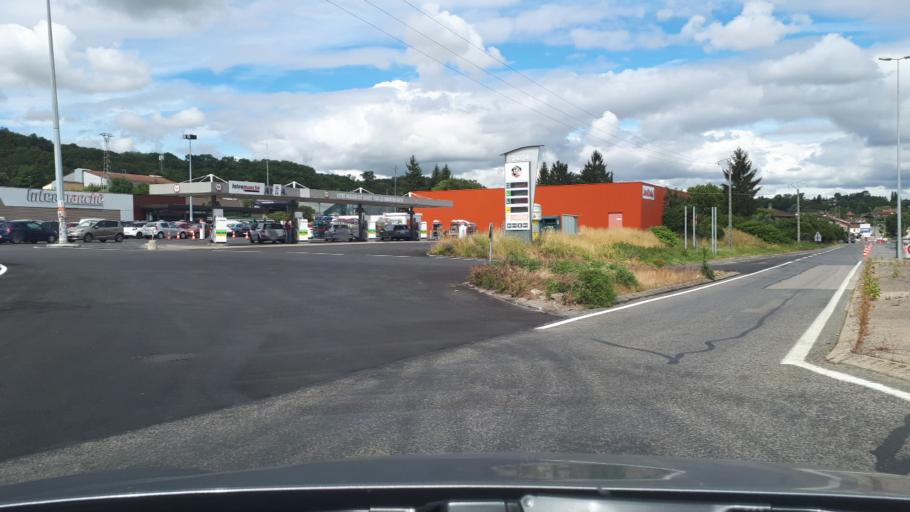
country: FR
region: Rhone-Alpes
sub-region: Departement de l'Isere
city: Domarin
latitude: 45.5905
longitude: 5.2426
